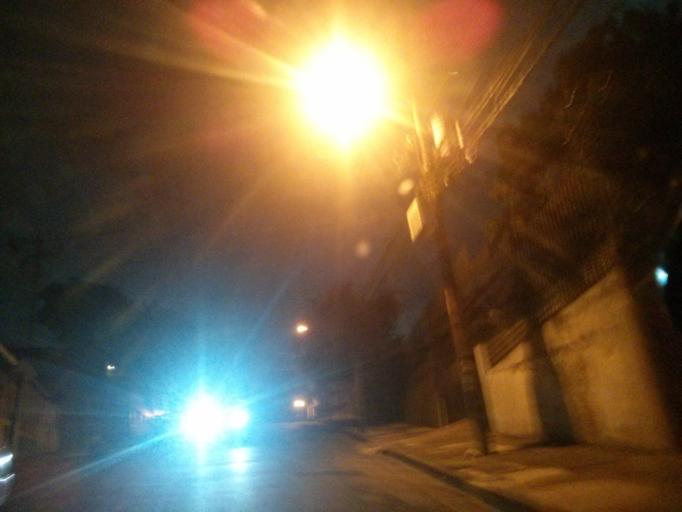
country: CR
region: San Jose
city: Colima
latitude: 9.9429
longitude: -84.0864
